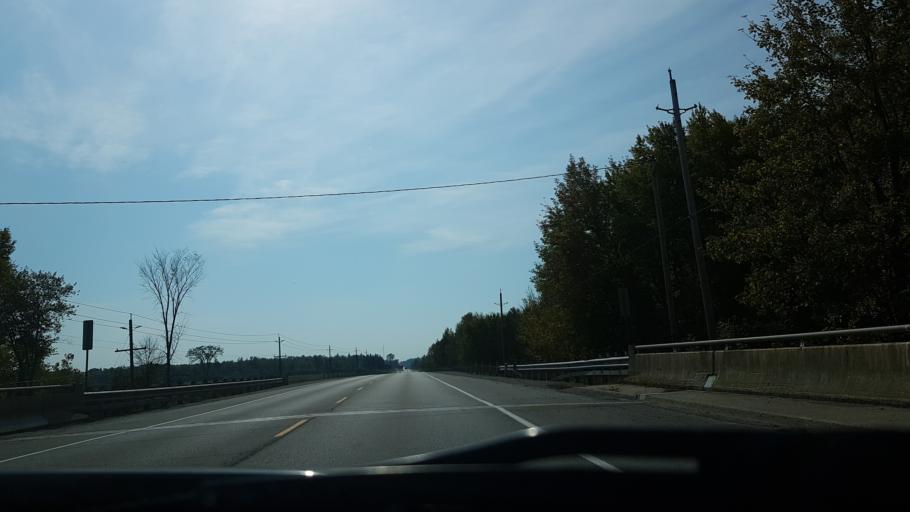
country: CA
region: Ontario
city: Orillia
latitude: 44.7139
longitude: -79.2817
